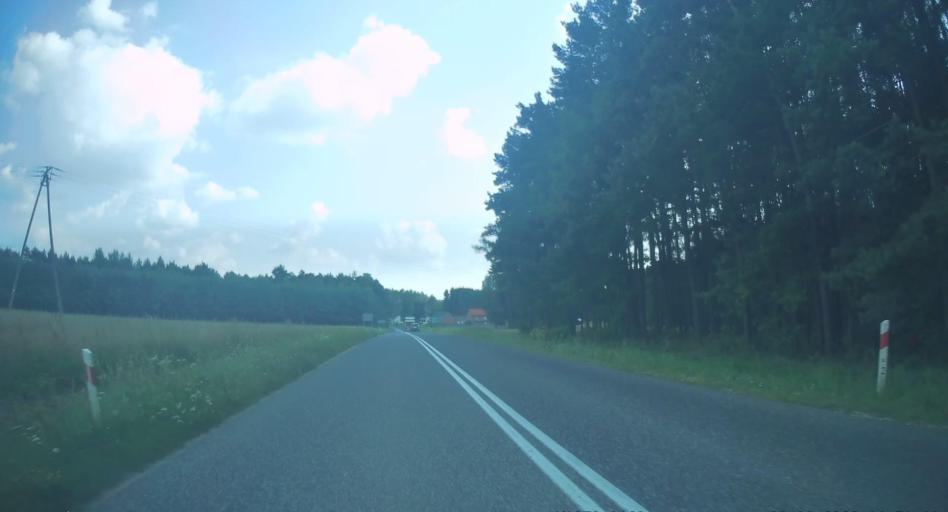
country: PL
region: Swietokrzyskie
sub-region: Powiat kielecki
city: Lopuszno
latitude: 50.8997
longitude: 20.2491
